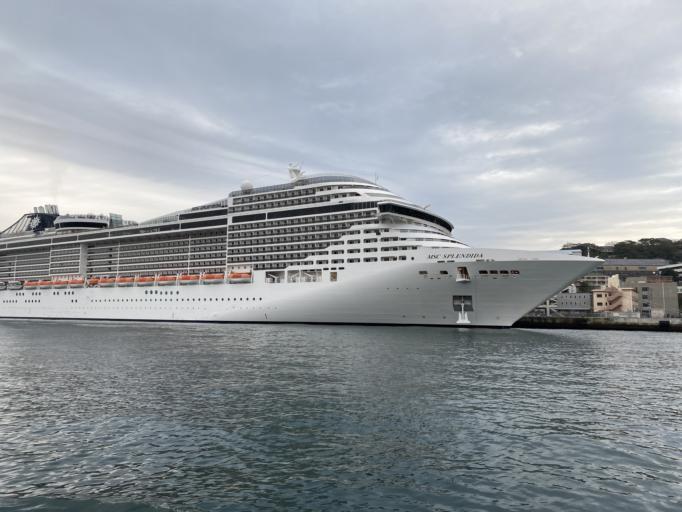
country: JP
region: Nagasaki
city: Nagasaki-shi
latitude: 32.7361
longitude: 129.8646
